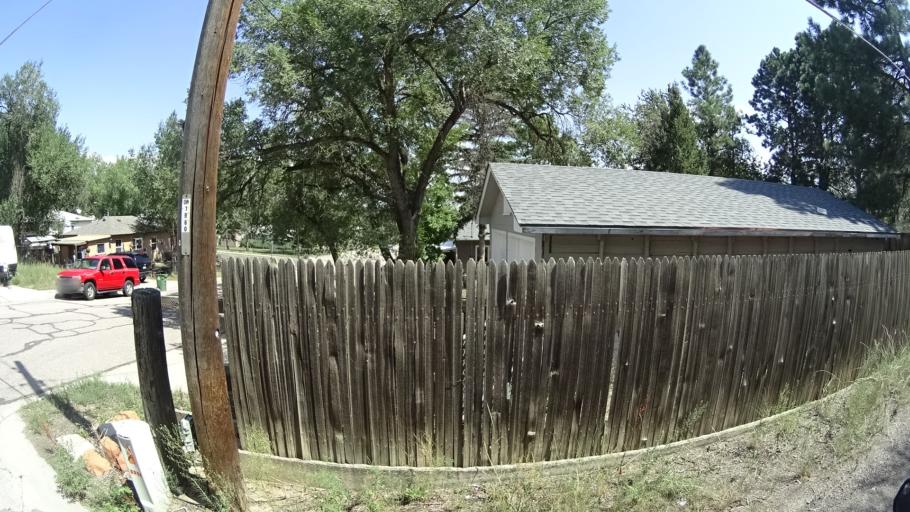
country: US
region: Colorado
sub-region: El Paso County
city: Colorado Springs
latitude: 38.8664
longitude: -104.8397
